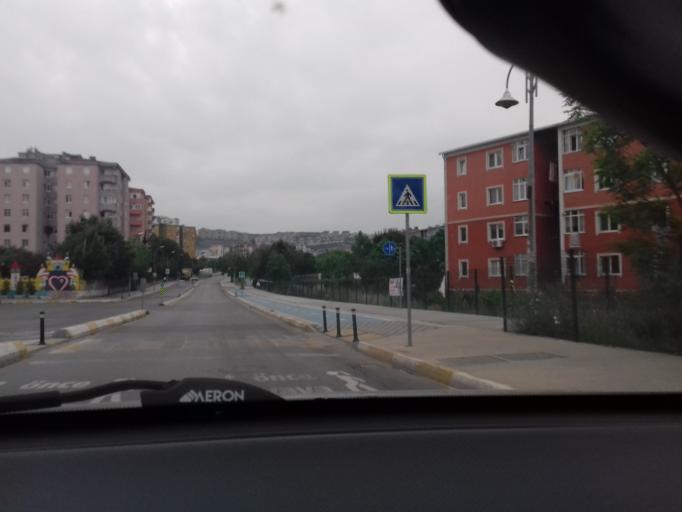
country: TR
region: Istanbul
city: Sultanbeyli
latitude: 40.9276
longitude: 29.2957
